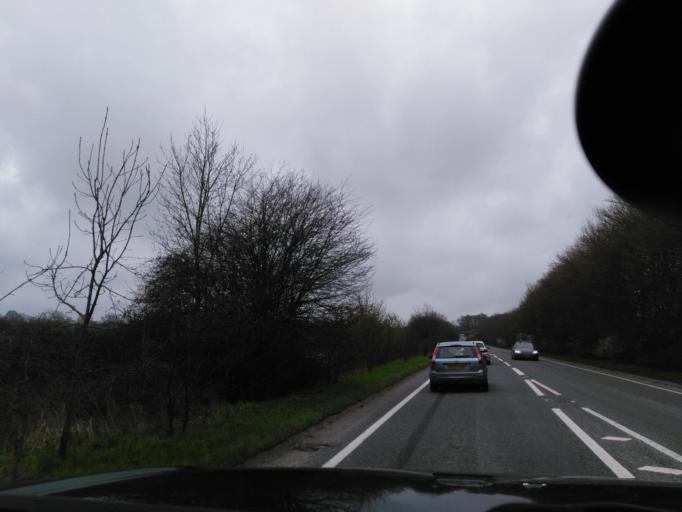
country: GB
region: England
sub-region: Somerset
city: Frome
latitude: 51.2142
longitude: -2.3090
